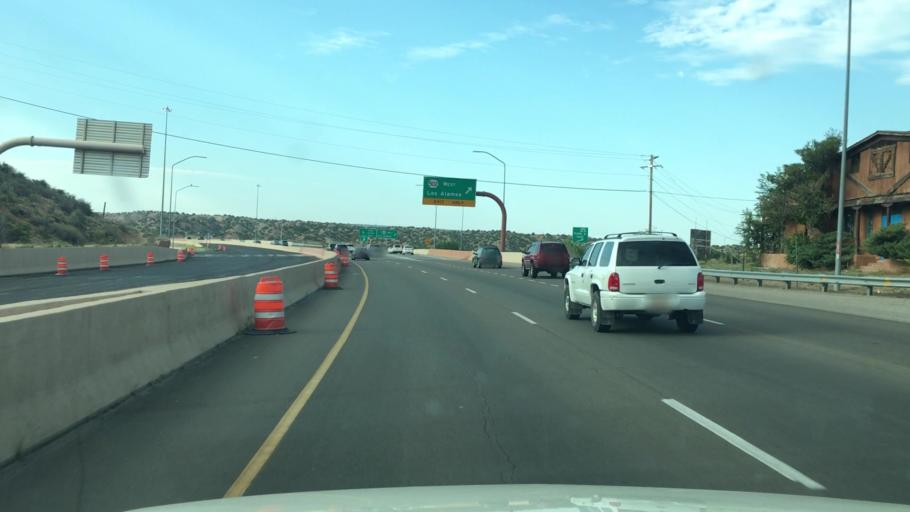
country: US
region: New Mexico
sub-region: Santa Fe County
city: Pojoaque
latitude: 35.8939
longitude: -106.0228
